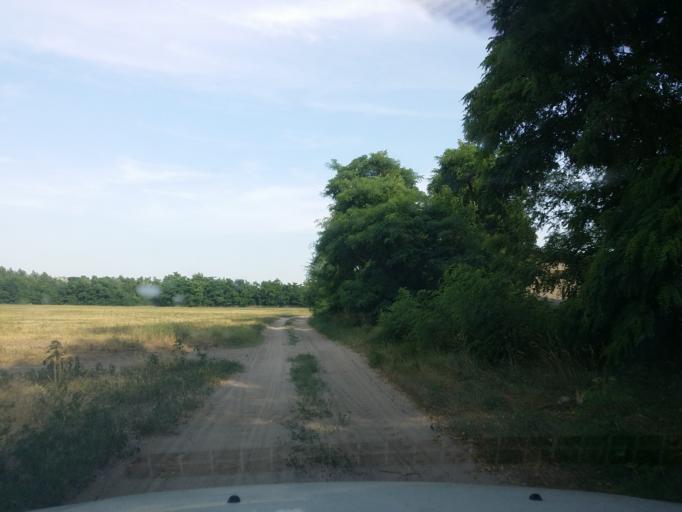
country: HU
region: Bacs-Kiskun
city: Jaszszentlaszlo
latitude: 46.5716
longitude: 19.7766
